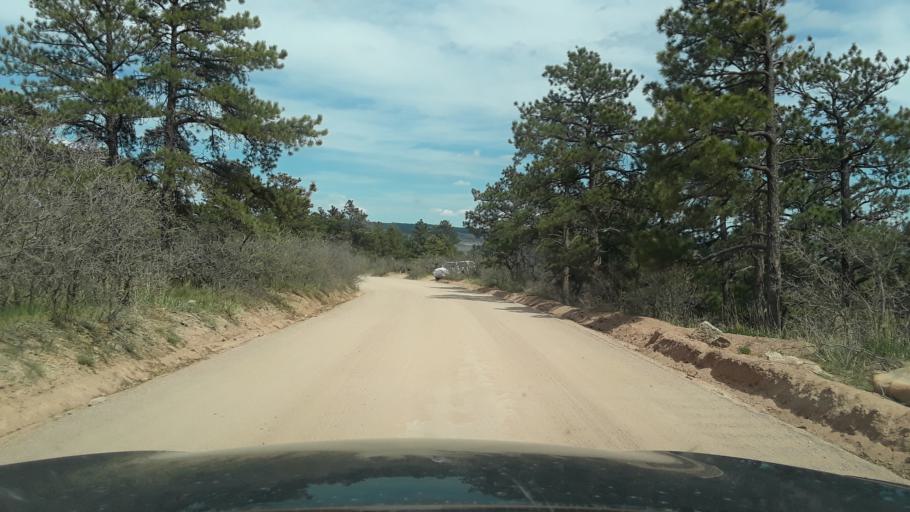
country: US
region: Colorado
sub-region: El Paso County
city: Monument
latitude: 39.0904
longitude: -104.9040
